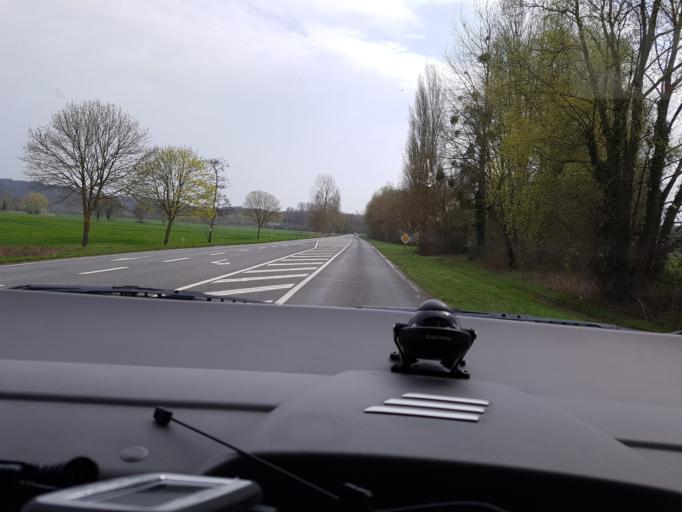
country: FR
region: Picardie
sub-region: Departement de l'Aisne
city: Coucy-le-Chateau-Auffrique
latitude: 49.5124
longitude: 3.3152
